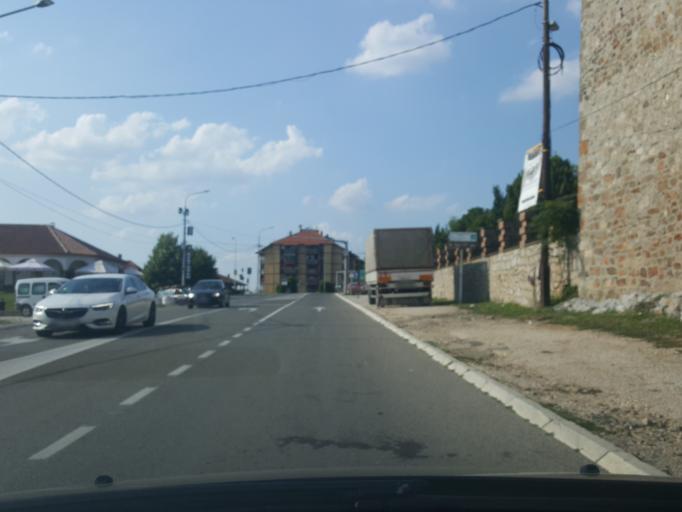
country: RS
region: Central Serbia
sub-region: Sumadijski Okrug
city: Topola
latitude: 44.2519
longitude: 20.6776
